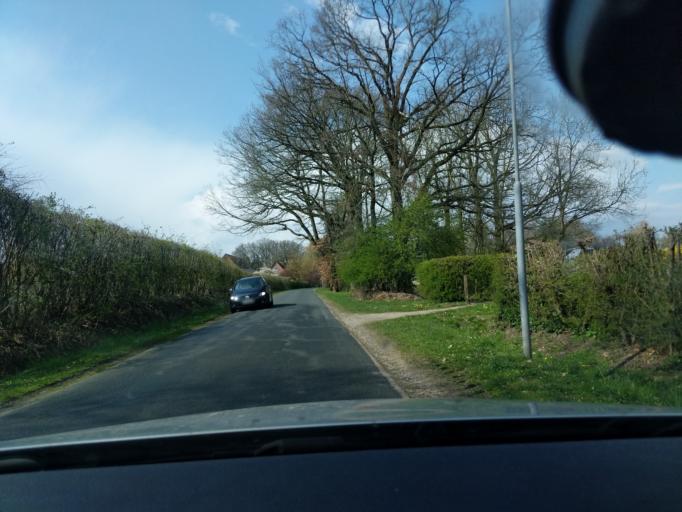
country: DE
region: Lower Saxony
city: Harsefeld
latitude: 53.4852
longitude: 9.5153
